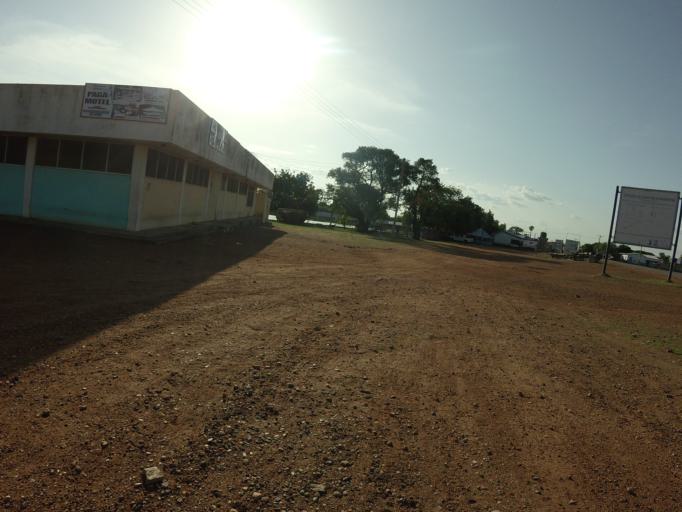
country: GH
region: Upper East
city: Navrongo
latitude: 10.9838
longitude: -1.1075
